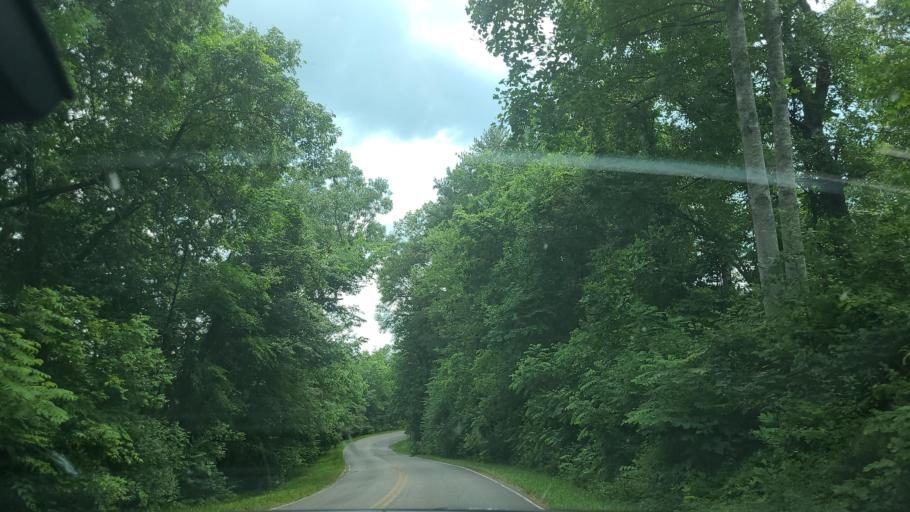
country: US
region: Tennessee
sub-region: Cumberland County
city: Lake Tansi
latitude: 35.8026
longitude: -85.0387
